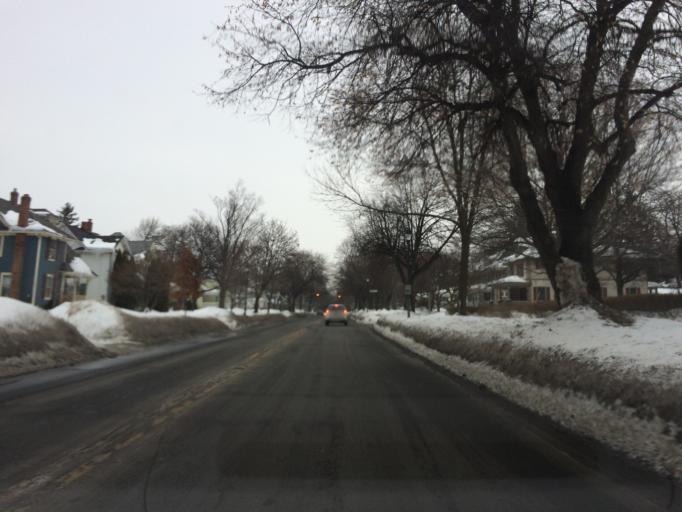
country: US
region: New York
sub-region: Monroe County
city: Fairport
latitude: 43.0987
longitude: -77.4491
